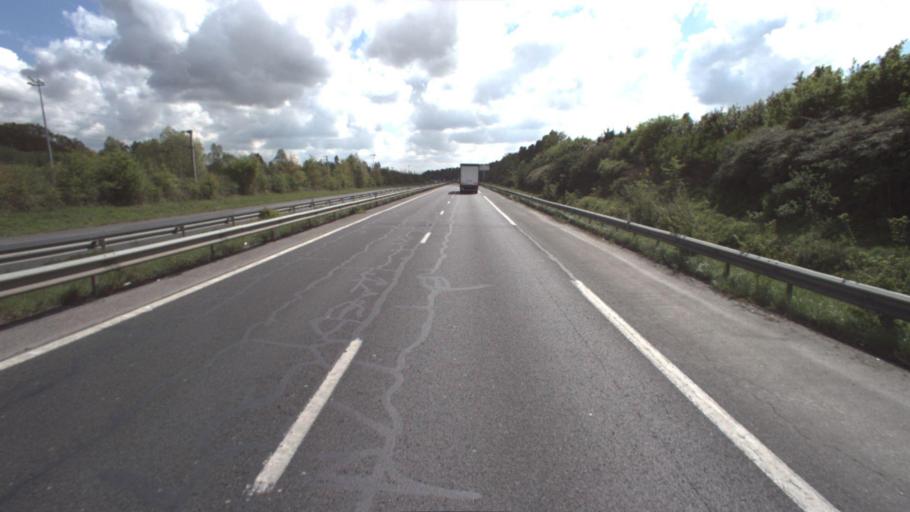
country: FR
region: Ile-de-France
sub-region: Departement de Seine-et-Marne
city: Tournan-en-Brie
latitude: 48.7305
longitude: 2.7963
